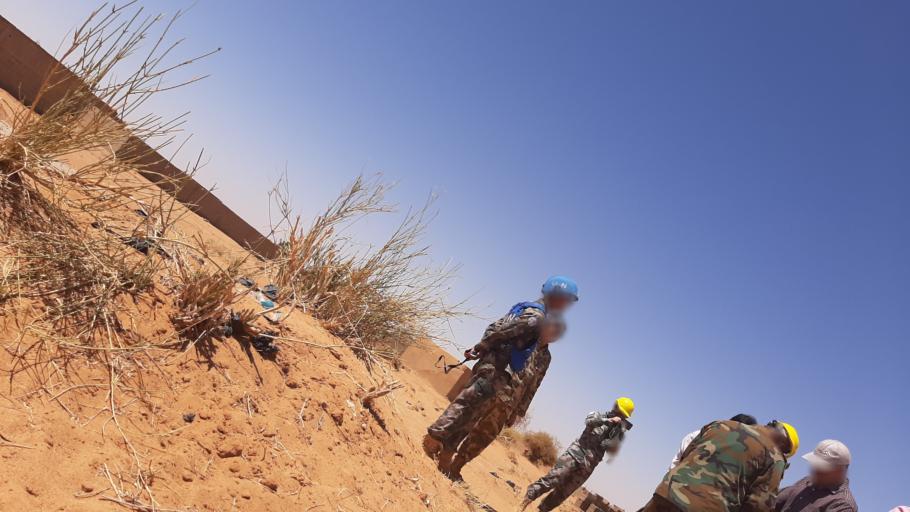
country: ML
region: Gao
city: Gao
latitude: 16.2438
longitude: -0.0251
